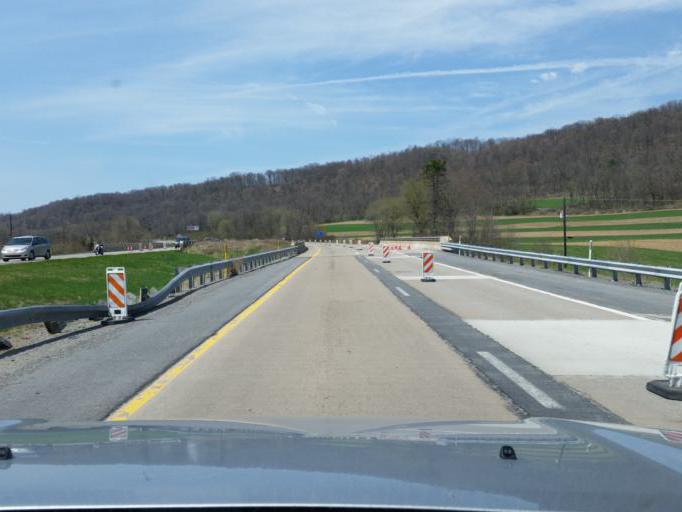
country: US
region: Pennsylvania
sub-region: Perry County
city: Newport
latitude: 40.5695
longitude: -77.2033
